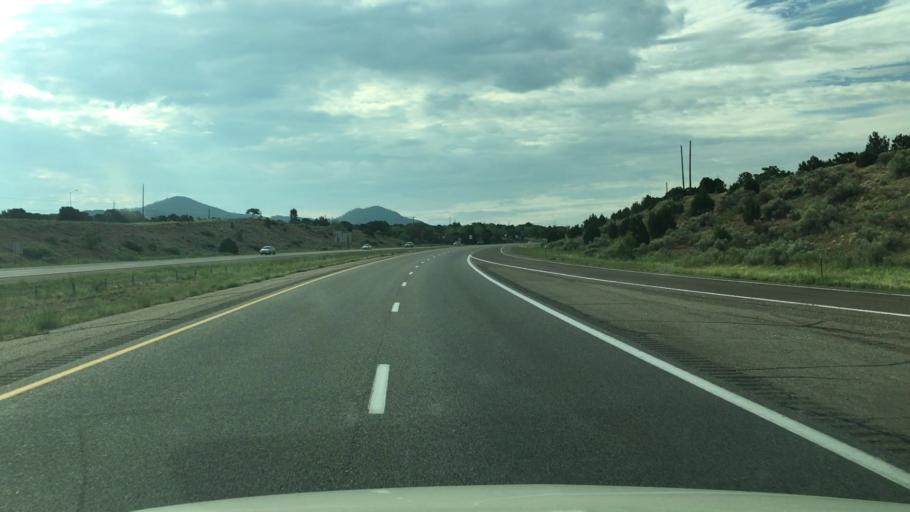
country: US
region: New Mexico
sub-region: Santa Fe County
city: Santa Fe
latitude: 35.6353
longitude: -105.9287
